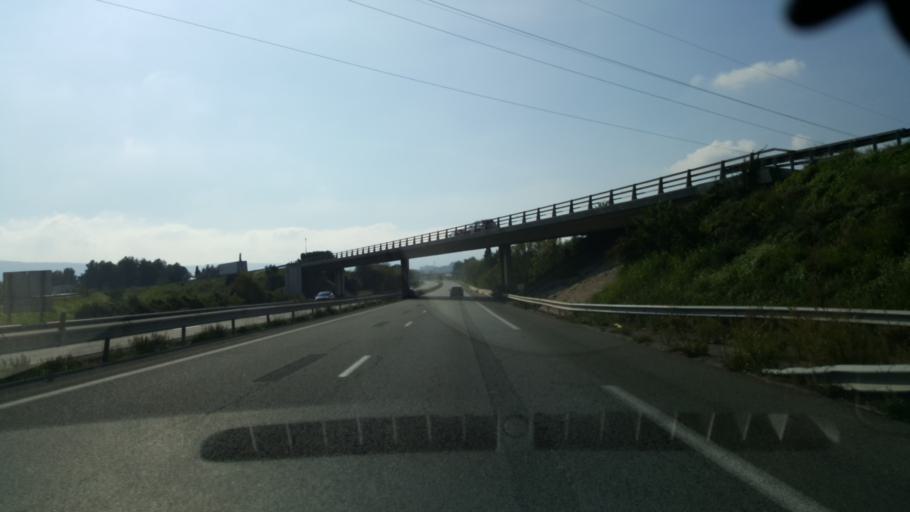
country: FR
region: Provence-Alpes-Cote d'Azur
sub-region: Departement des Bouches-du-Rhone
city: Roquevaire
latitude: 43.3194
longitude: 5.5918
